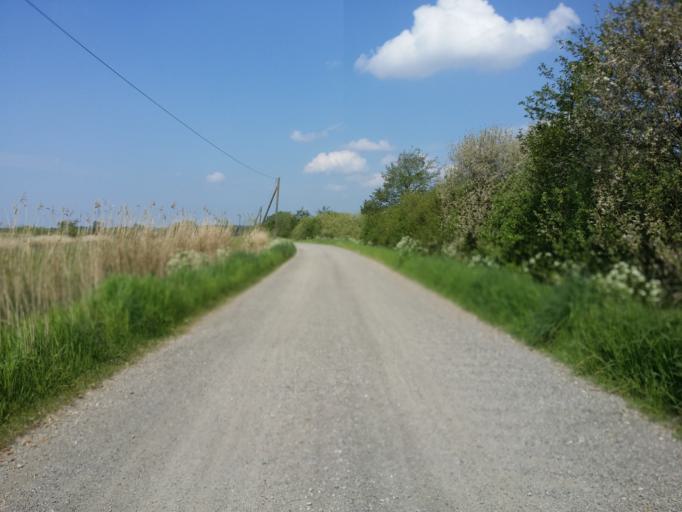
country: DE
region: Lower Saxony
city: Osterholz-Scharmbeck
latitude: 53.2203
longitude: 8.8483
